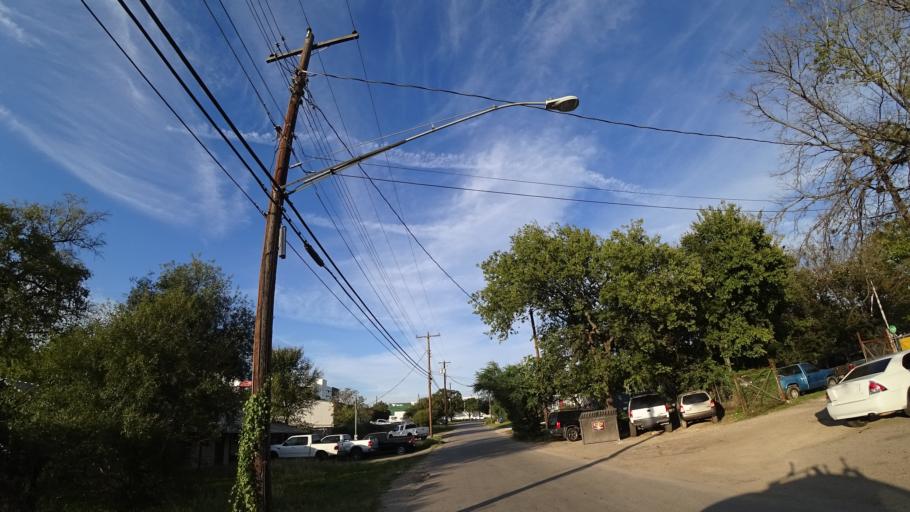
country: US
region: Texas
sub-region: Travis County
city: Austin
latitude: 30.2155
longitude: -97.7662
